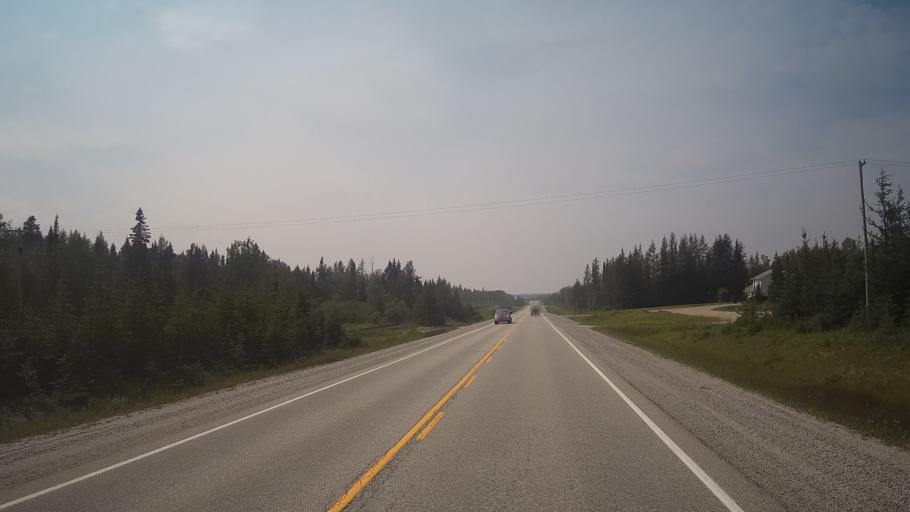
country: CA
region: Ontario
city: Kapuskasing
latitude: 49.3245
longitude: -82.0685
